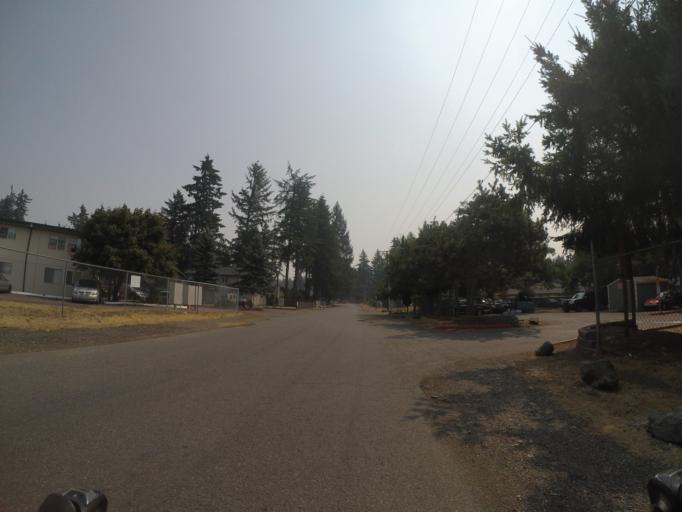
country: US
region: Washington
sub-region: Pierce County
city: McChord Air Force Base
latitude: 47.1416
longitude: -122.5118
